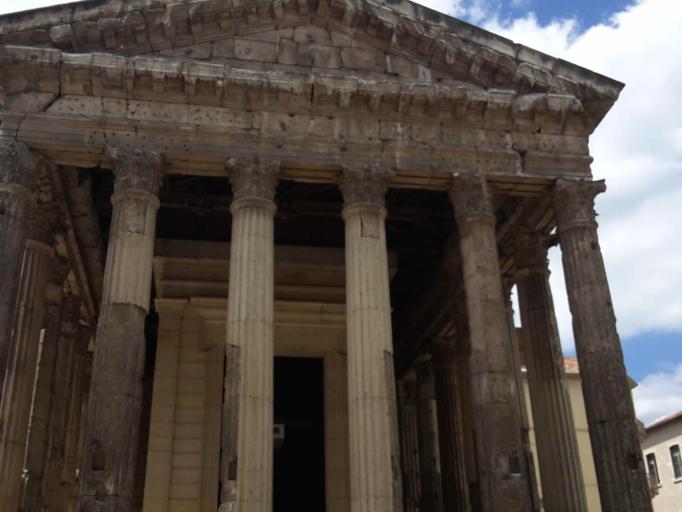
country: FR
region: Rhone-Alpes
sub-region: Departement de l'Isere
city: Vienne
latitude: 45.5255
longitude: 4.8746
